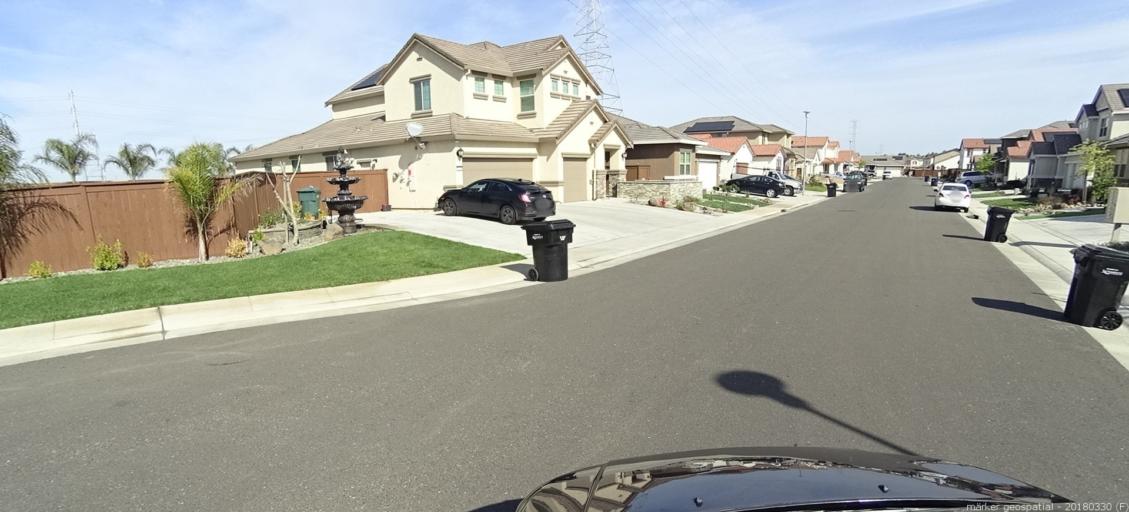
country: US
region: California
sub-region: Sacramento County
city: Vineyard
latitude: 38.4874
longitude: -121.3496
